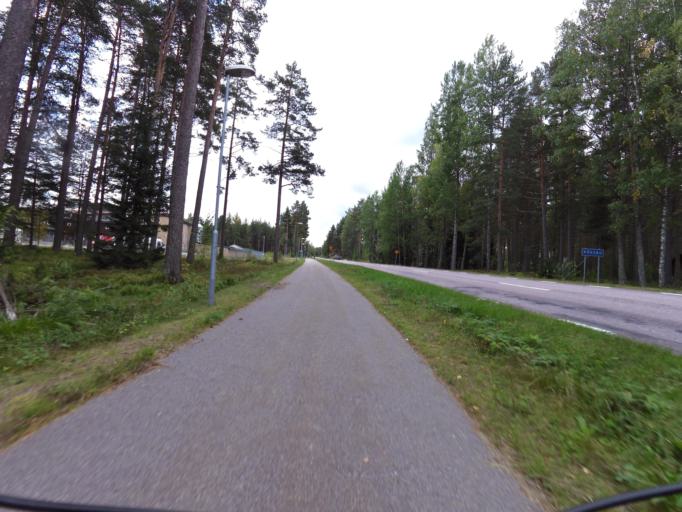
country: SE
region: Gaevleborg
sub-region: Sandvikens Kommun
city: Sandviken
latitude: 60.6887
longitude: 16.8146
